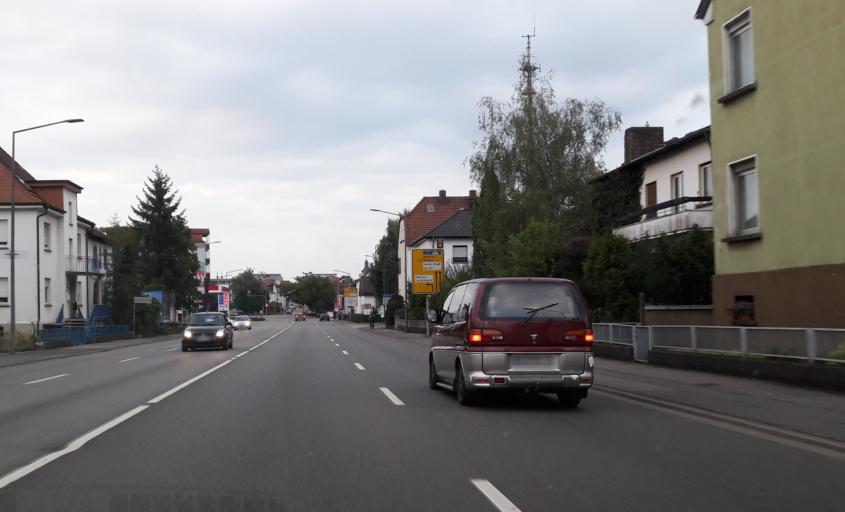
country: DE
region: Saarland
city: Homburg
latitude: 49.3140
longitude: 7.3359
